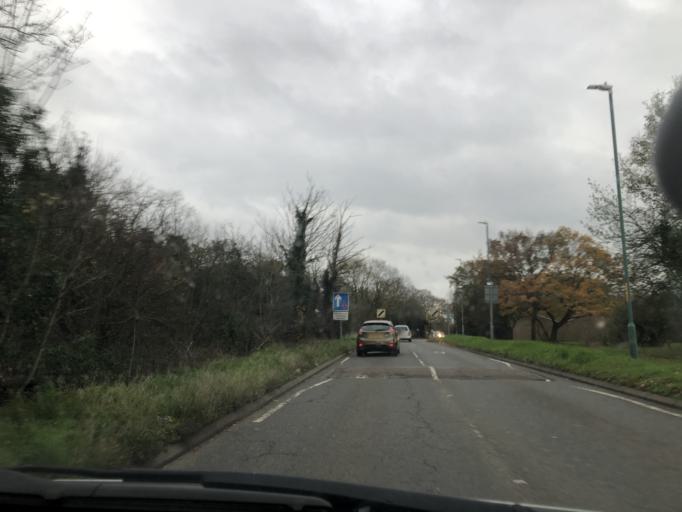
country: GB
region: England
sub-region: Greater London
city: Bexley
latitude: 51.4427
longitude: 0.1806
